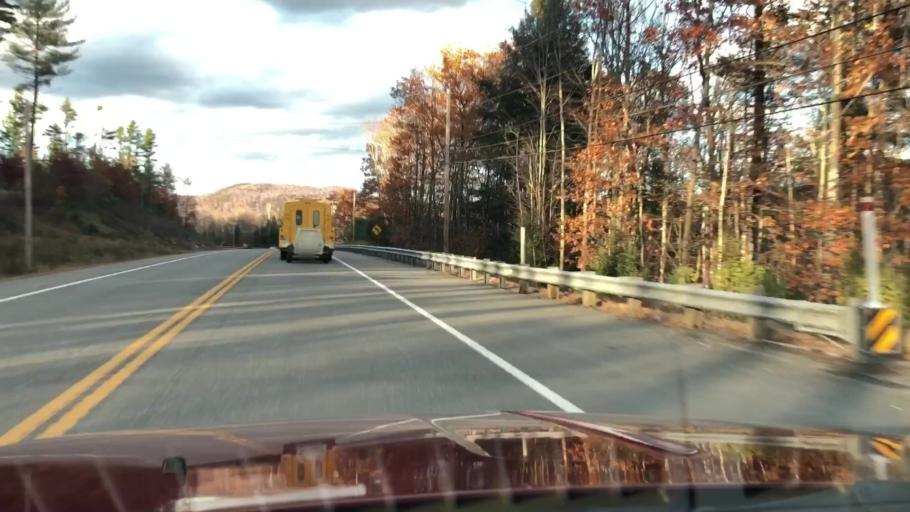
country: US
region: Maine
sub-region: Oxford County
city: Peru
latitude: 44.5289
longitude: -70.4062
